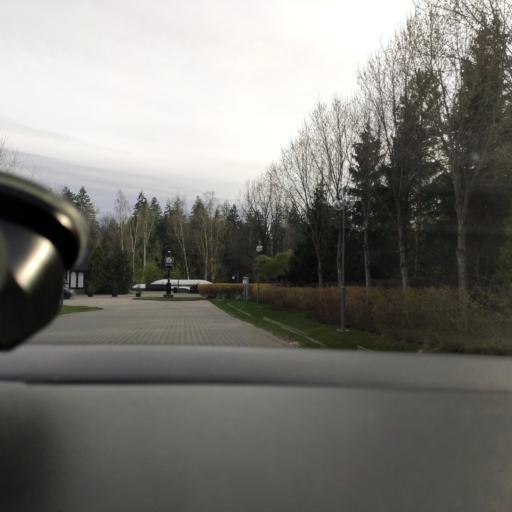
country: RU
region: Moskovskaya
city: Zhavoronki
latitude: 55.6907
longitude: 37.0937
